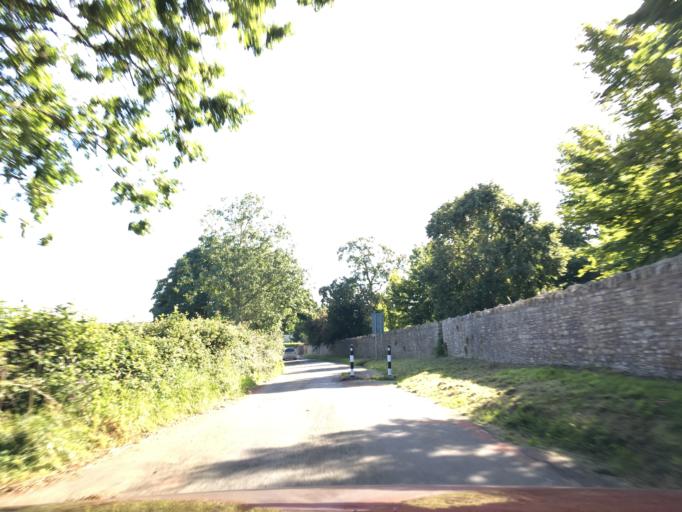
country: GB
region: England
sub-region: Bath and North East Somerset
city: Publow
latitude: 51.3999
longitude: -2.5294
